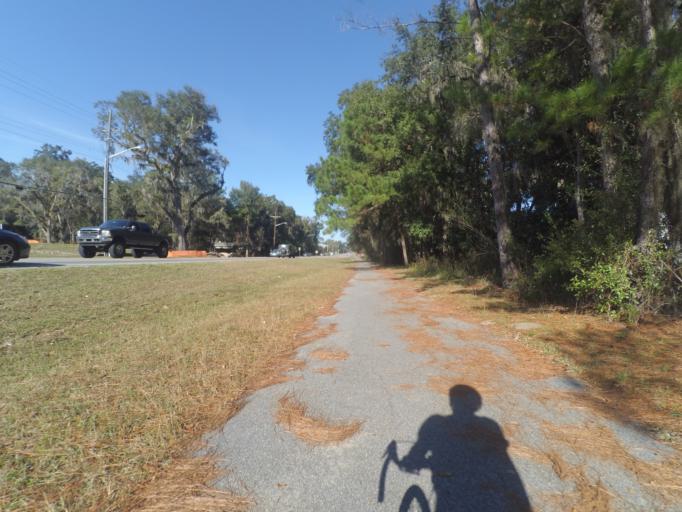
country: US
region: Florida
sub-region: Alachua County
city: Gainesville
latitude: 29.6264
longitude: -82.4224
